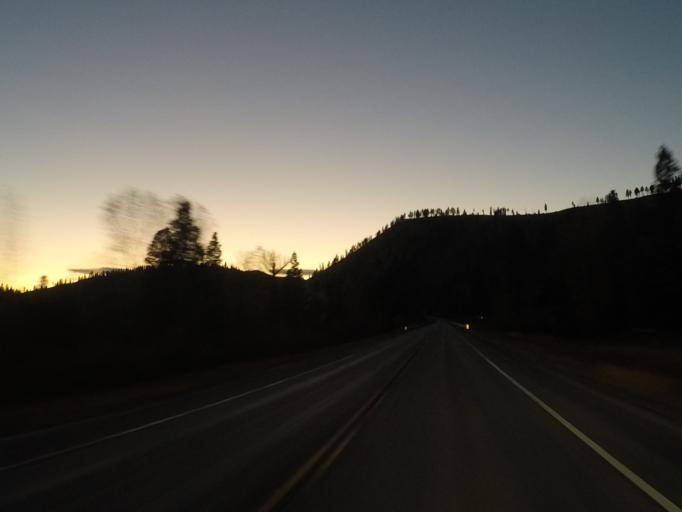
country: US
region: Montana
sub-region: Missoula County
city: Seeley Lake
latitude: 47.0231
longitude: -113.2972
